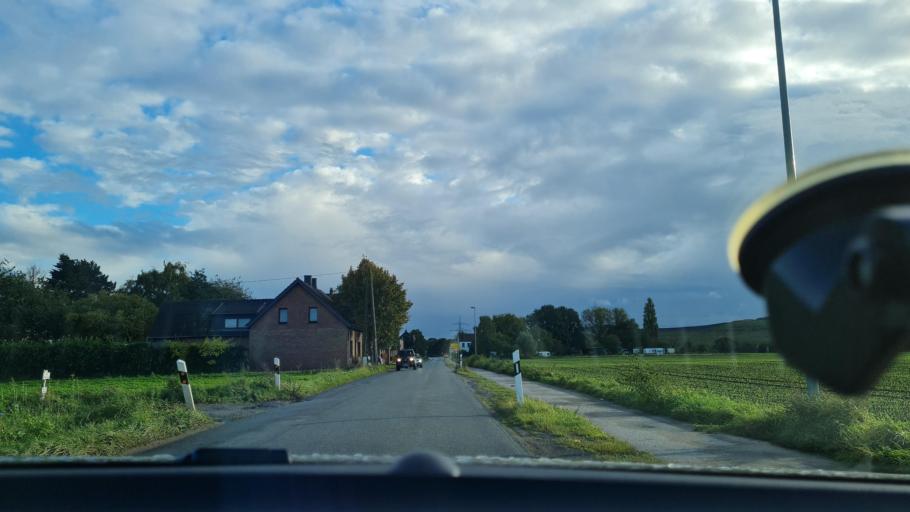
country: DE
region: North Rhine-Westphalia
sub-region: Regierungsbezirk Dusseldorf
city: Dinslaken
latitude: 51.5508
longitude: 6.7687
